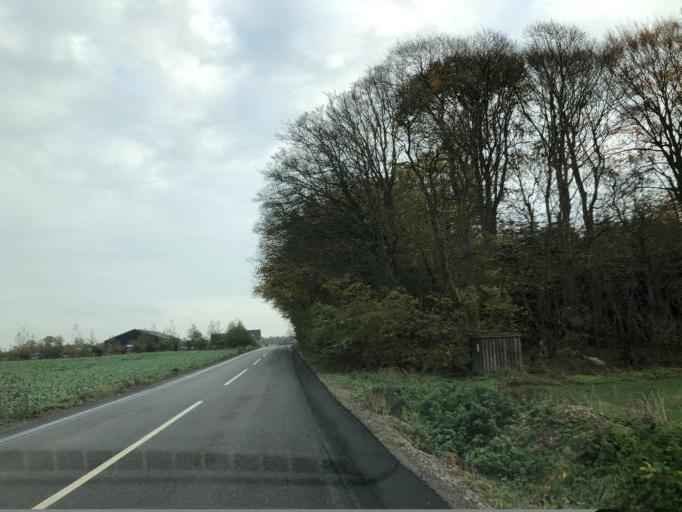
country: DK
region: Central Jutland
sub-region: Hedensted Kommune
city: Hornsyld
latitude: 55.7373
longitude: 9.8040
